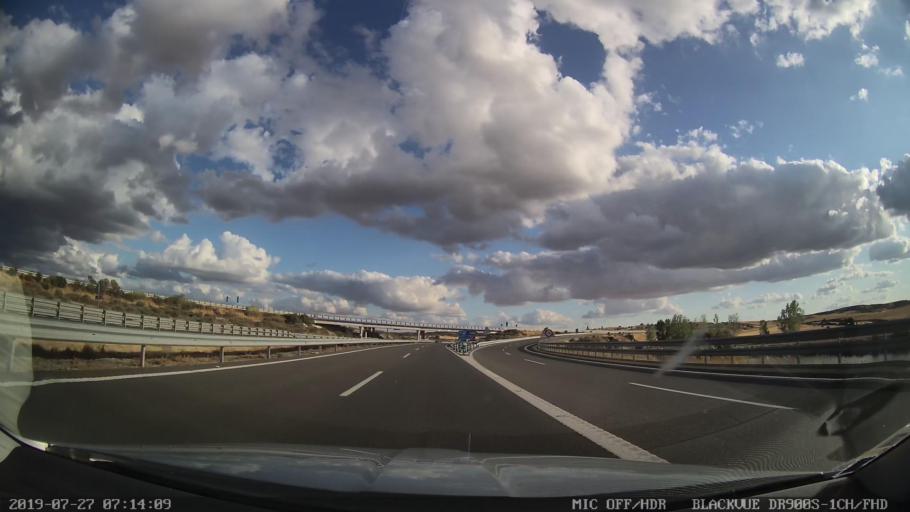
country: ES
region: Extremadura
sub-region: Provincia de Caceres
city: Trujillo
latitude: 39.4982
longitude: -5.8410
